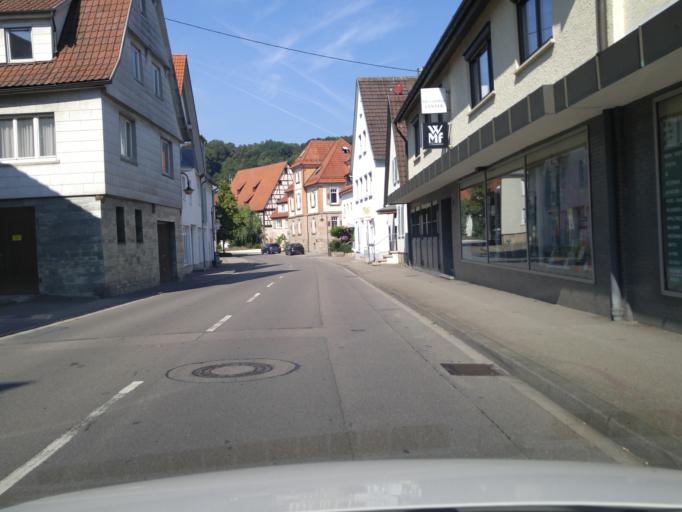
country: DE
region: Baden-Wuerttemberg
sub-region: Regierungsbezirk Stuttgart
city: Neckartenzlingen
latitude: 48.5909
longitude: 9.2364
